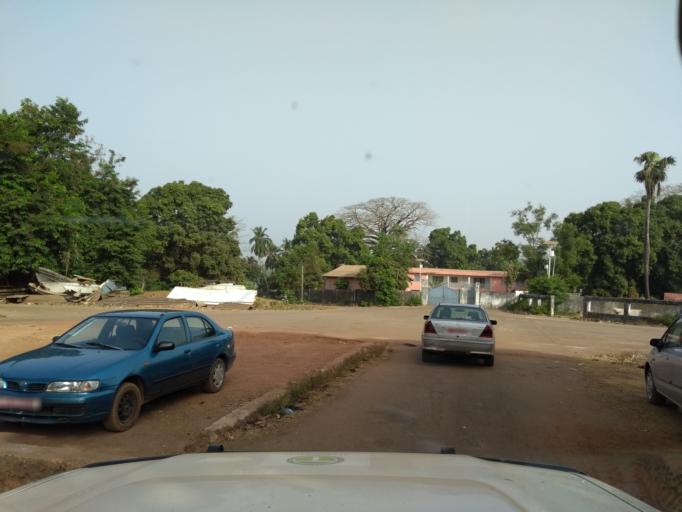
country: GN
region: Kindia
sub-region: Prefecture de Dubreka
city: Dubreka
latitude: 9.7924
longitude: -13.5234
